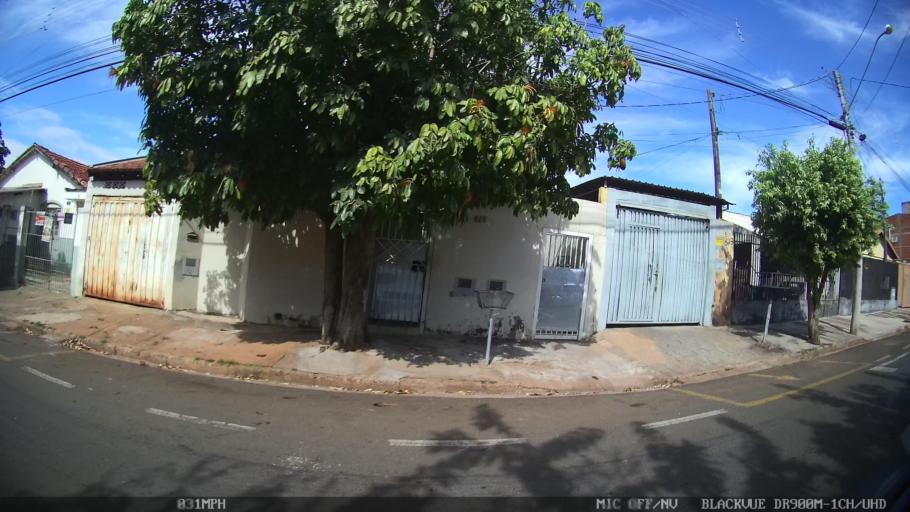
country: BR
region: Sao Paulo
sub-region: Sao Jose Do Rio Preto
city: Sao Jose do Rio Preto
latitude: -20.8432
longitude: -49.3445
